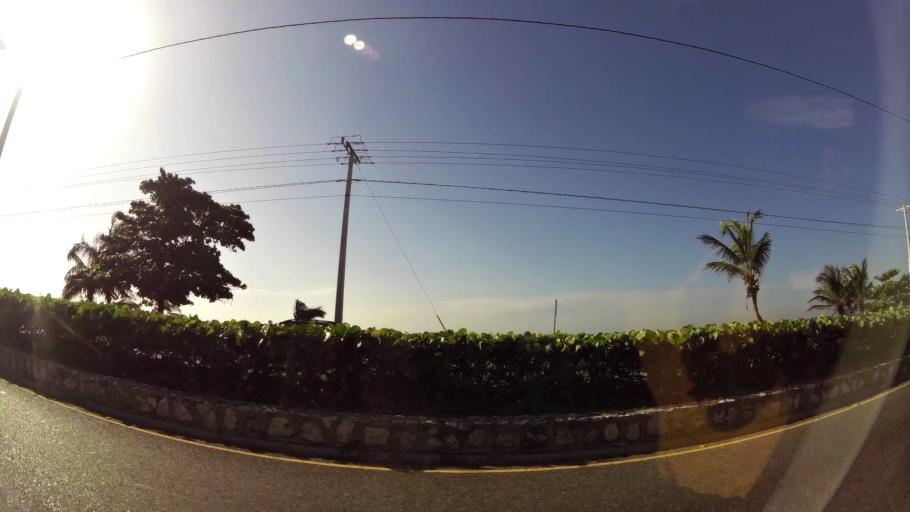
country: DO
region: Santo Domingo
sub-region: Santo Domingo
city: Santo Domingo Este
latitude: 18.4674
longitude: -69.8699
